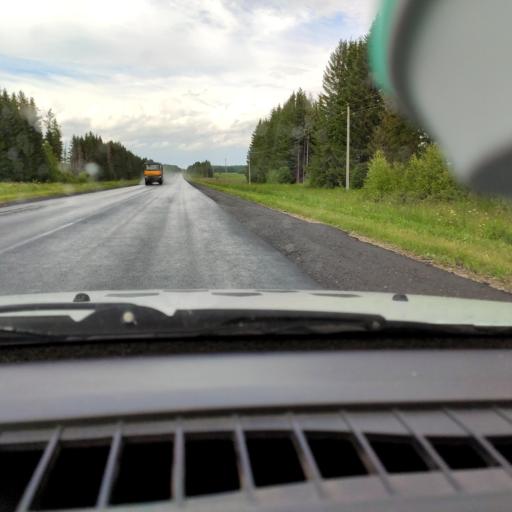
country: RU
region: Perm
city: Orda
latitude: 57.2118
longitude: 56.9363
